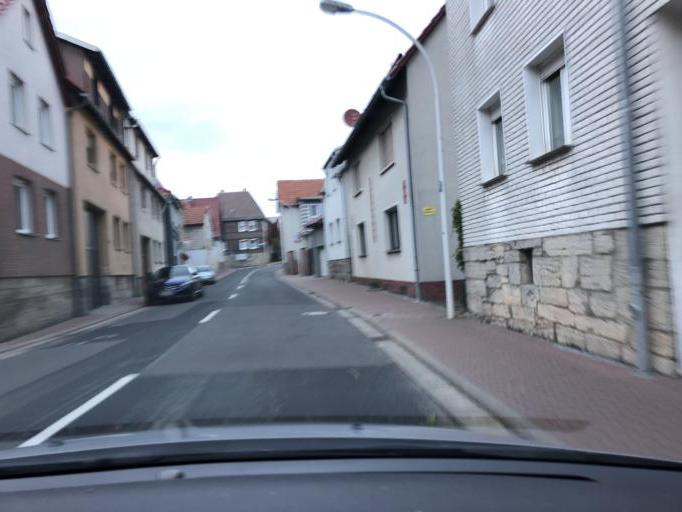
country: DE
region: Thuringia
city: Buttstedt
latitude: 51.2238
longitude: 10.3031
